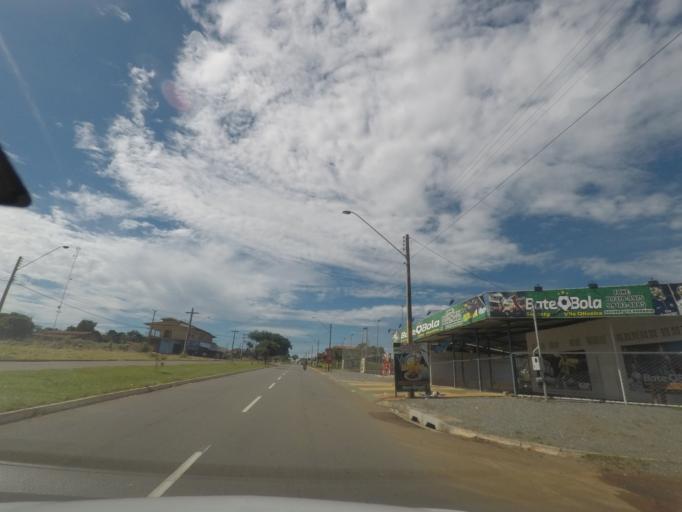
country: BR
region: Goias
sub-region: Aparecida De Goiania
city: Aparecida de Goiania
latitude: -16.7996
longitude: -49.2834
